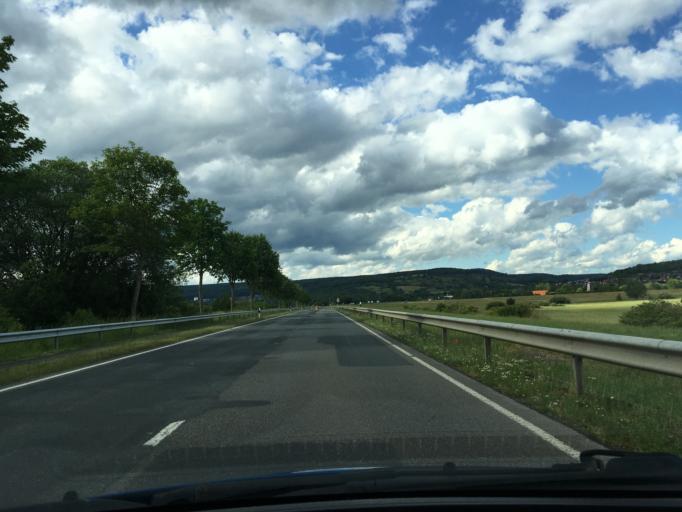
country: DE
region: Lower Saxony
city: Einbeck
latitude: 51.7909
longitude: 9.8982
